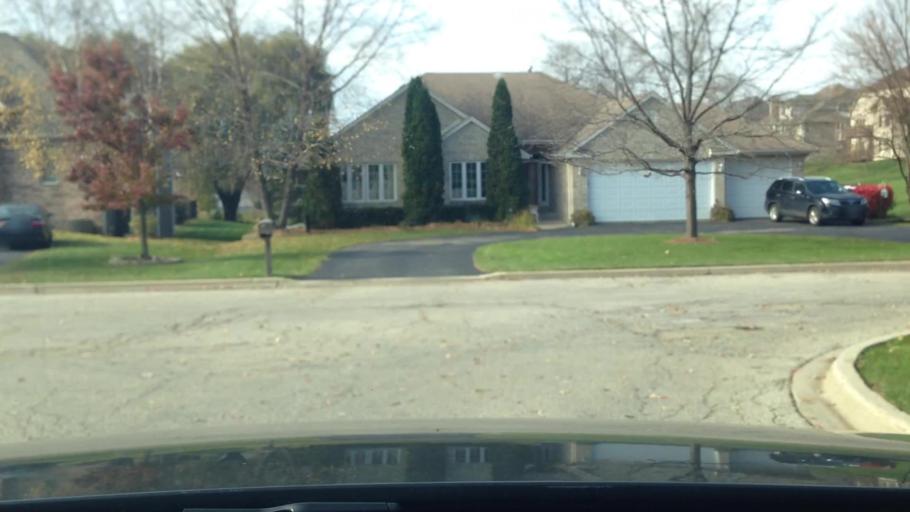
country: US
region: Illinois
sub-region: McHenry County
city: Woodstock
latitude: 42.3001
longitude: -88.4775
